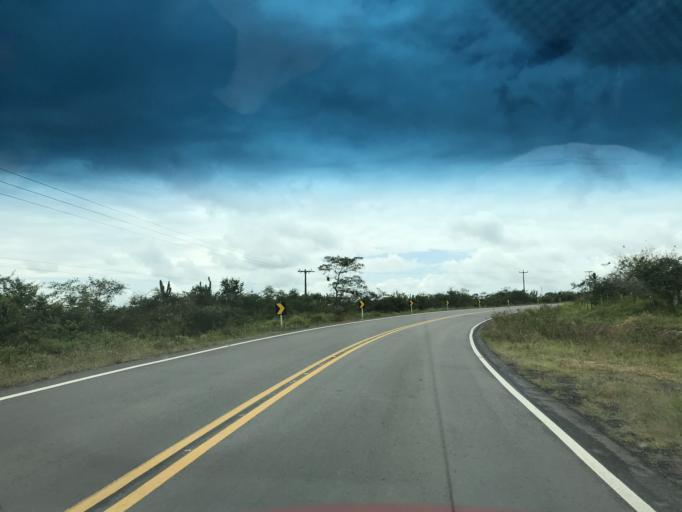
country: BR
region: Bahia
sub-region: Conceicao Do Almeida
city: Conceicao do Almeida
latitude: -12.6668
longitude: -39.2843
